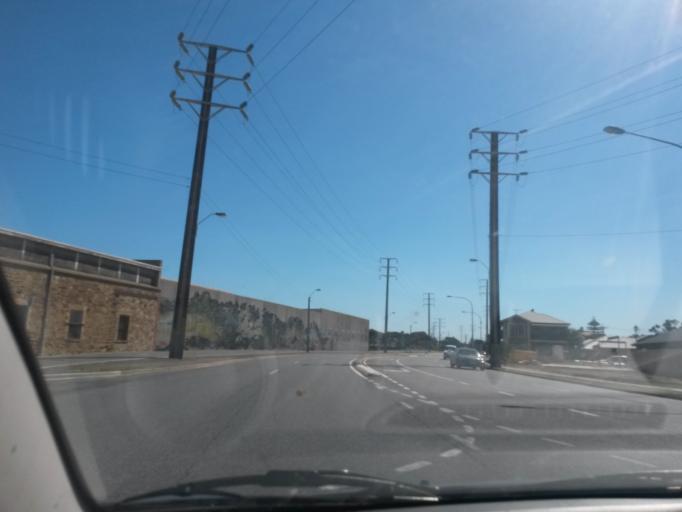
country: AU
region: South Australia
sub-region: Port Adelaide Enfield
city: Birkenhead
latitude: -34.8399
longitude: 138.4983
